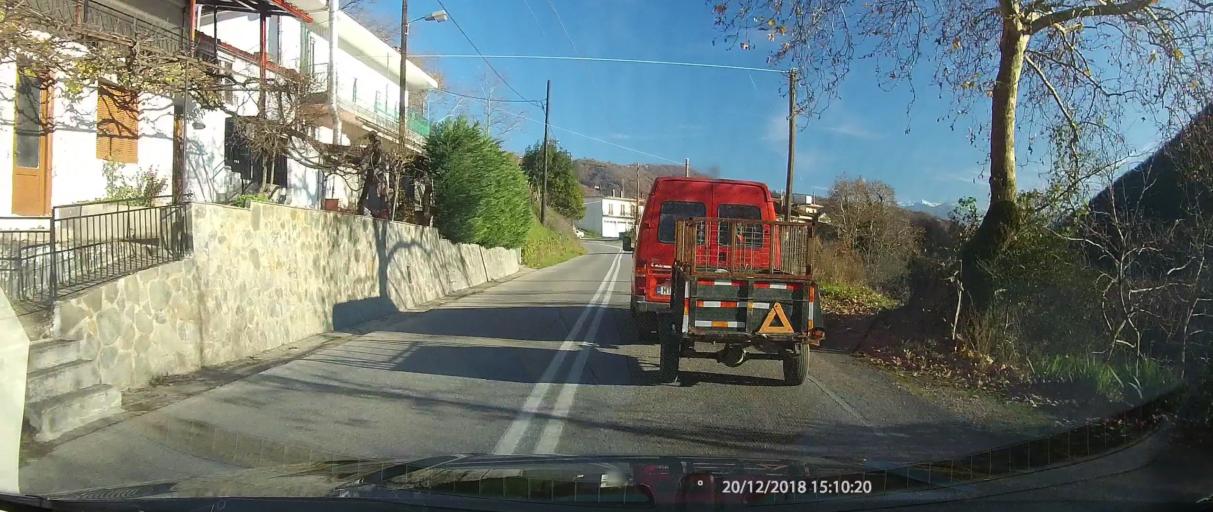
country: GR
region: Central Greece
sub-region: Nomos Fthiotidos
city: Makrakomi
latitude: 38.9478
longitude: 21.9515
